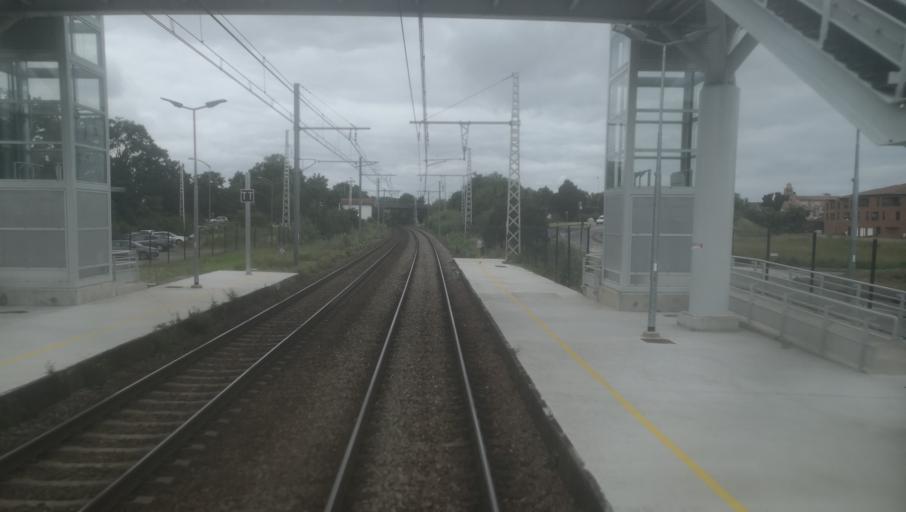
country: FR
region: Midi-Pyrenees
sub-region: Departement de la Haute-Garonne
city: Saint-Jory
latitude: 43.7386
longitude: 1.3712
